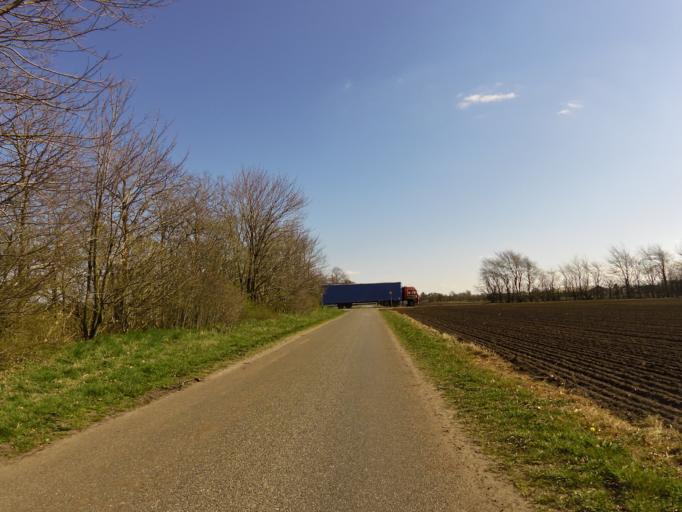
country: DK
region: South Denmark
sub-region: Esbjerg Kommune
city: Ribe
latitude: 55.3373
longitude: 8.8783
